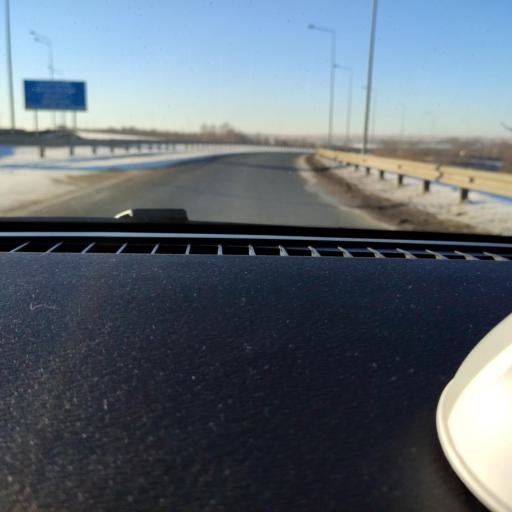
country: RU
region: Samara
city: Smyshlyayevka
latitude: 53.1369
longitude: 50.4296
